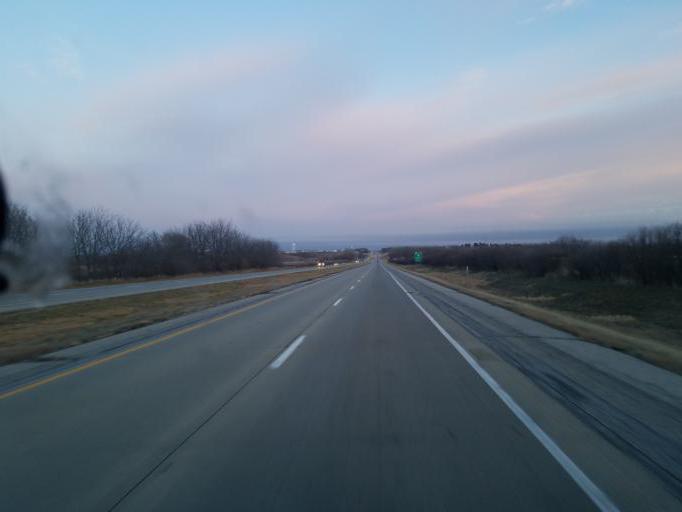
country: US
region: Iowa
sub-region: Pottawattamie County
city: Avoca
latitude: 41.4975
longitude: -95.3662
